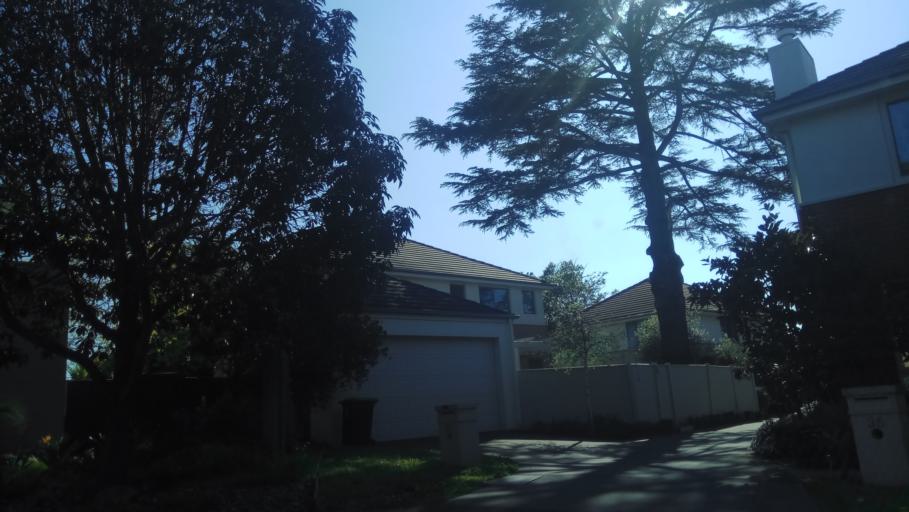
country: AU
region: Victoria
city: Heatherton
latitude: -37.9543
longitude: 145.0827
